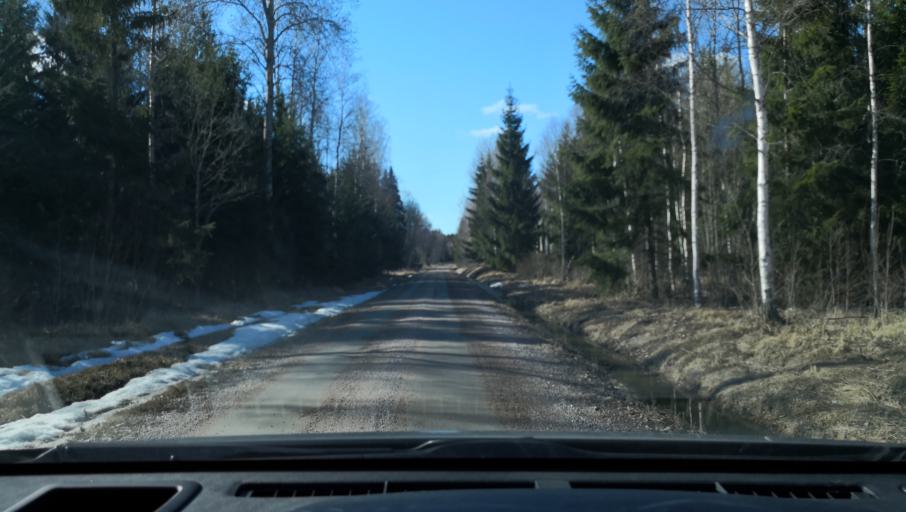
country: SE
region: Vaestmanland
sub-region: Sala Kommun
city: Sala
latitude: 60.1148
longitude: 16.6782
